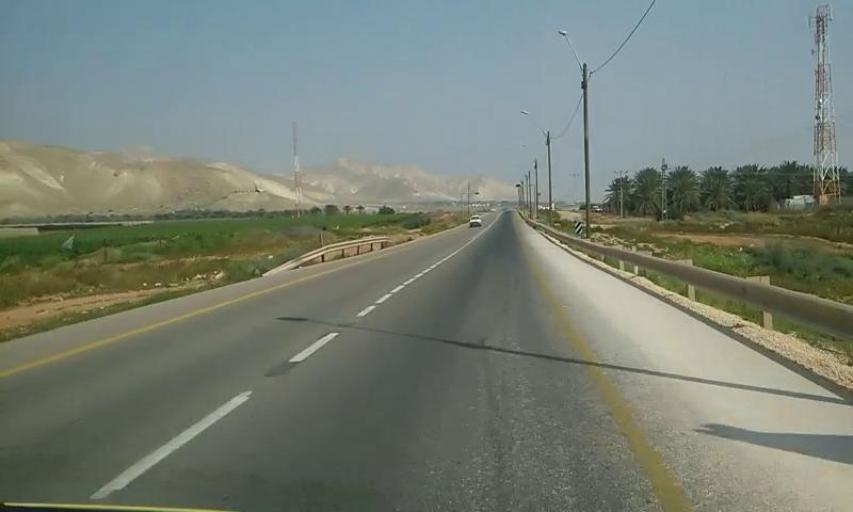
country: PS
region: West Bank
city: Al Fasayil
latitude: 32.0413
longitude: 35.4594
